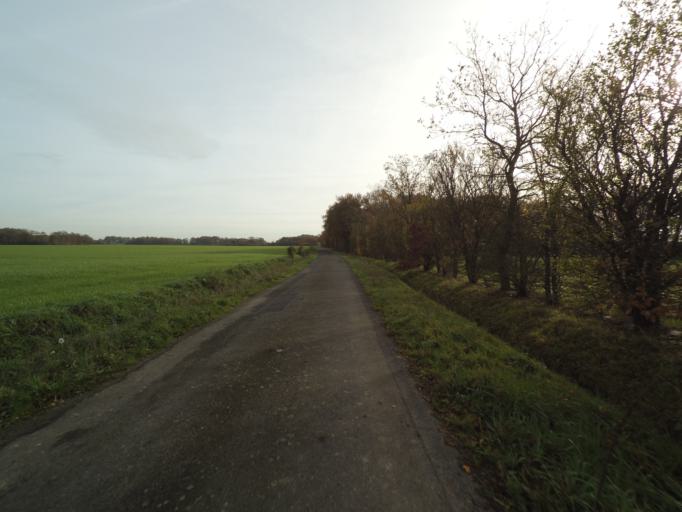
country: FR
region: Pays de la Loire
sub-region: Departement de la Loire-Atlantique
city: La Planche
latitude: 47.0104
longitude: -1.4080
